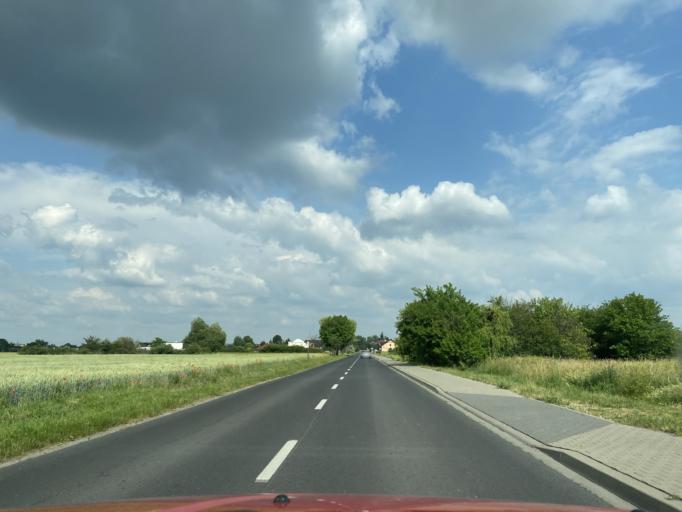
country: PL
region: Greater Poland Voivodeship
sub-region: Powiat poznanski
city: Dopiewo
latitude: 52.3599
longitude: 16.6996
